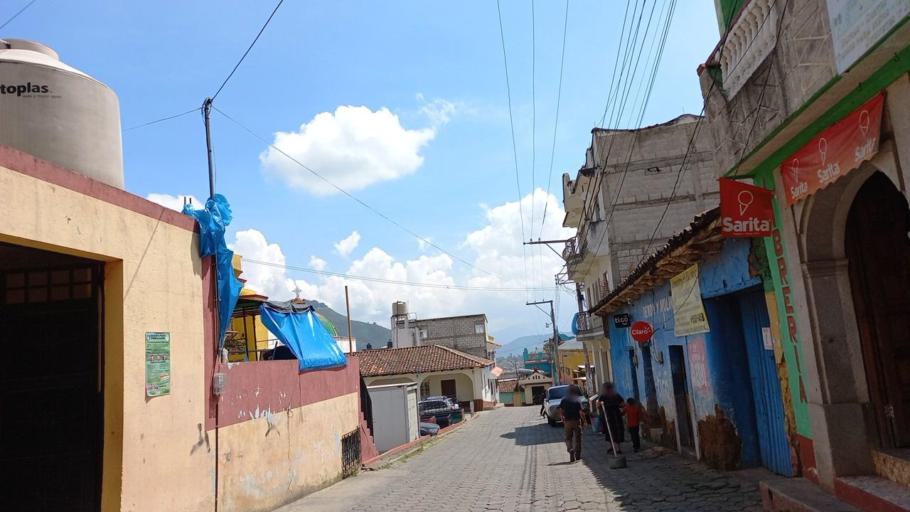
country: GT
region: Totonicapan
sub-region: Municipio de San Andres Xecul
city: San Andres Xecul
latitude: 14.9043
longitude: -91.4832
